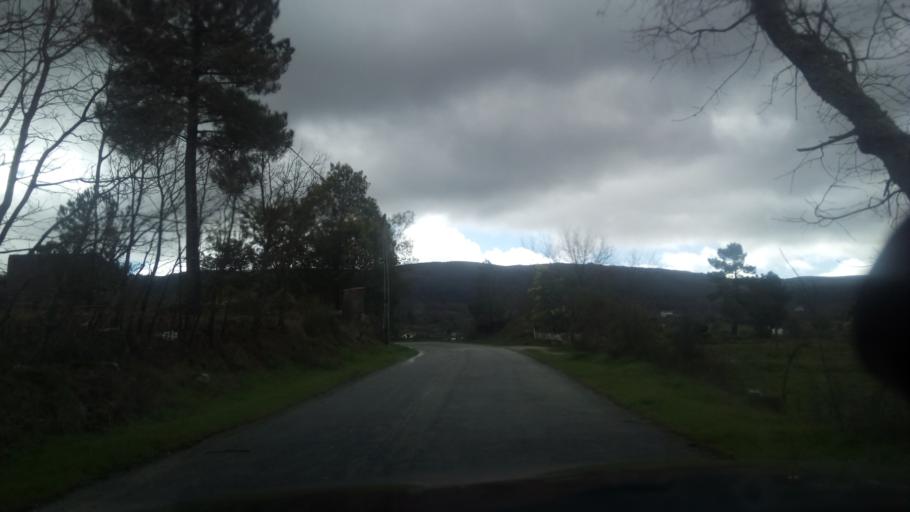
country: PT
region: Guarda
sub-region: Celorico da Beira
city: Celorico da Beira
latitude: 40.5621
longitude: -7.4583
